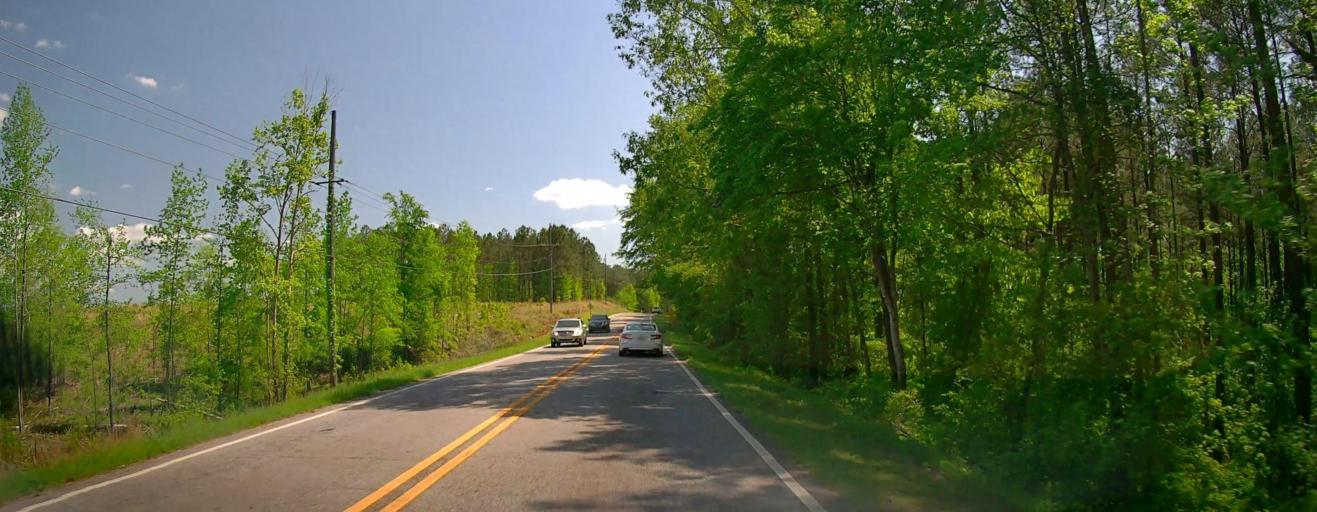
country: US
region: Georgia
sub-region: Putnam County
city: Eatonton
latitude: 33.2492
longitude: -83.3036
